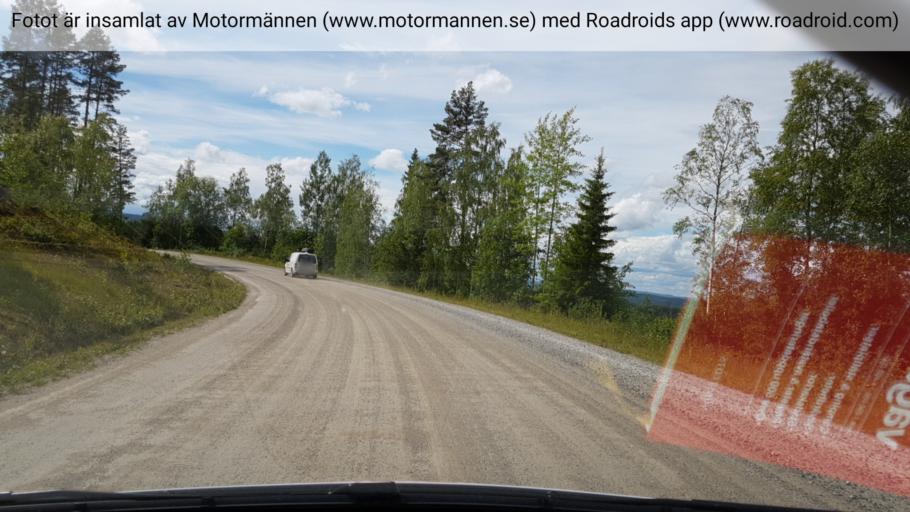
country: SE
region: Vaesternorrland
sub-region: Solleftea Kommun
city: Solleftea
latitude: 63.3187
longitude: 17.2368
